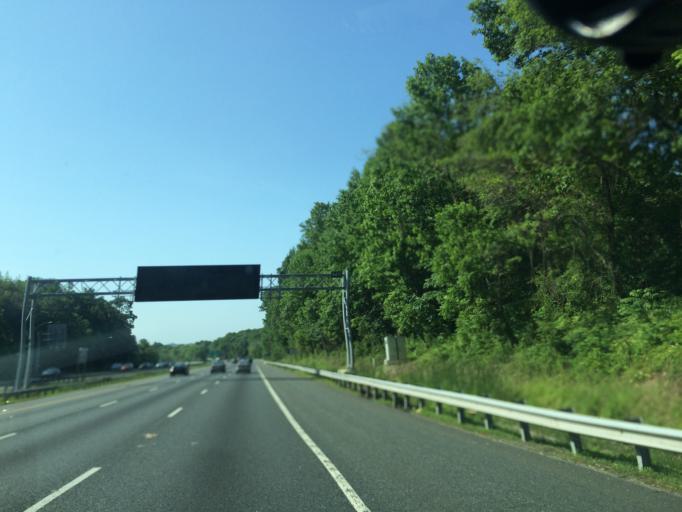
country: US
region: Maryland
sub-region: Baltimore County
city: Overlea
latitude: 39.3782
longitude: -76.5196
